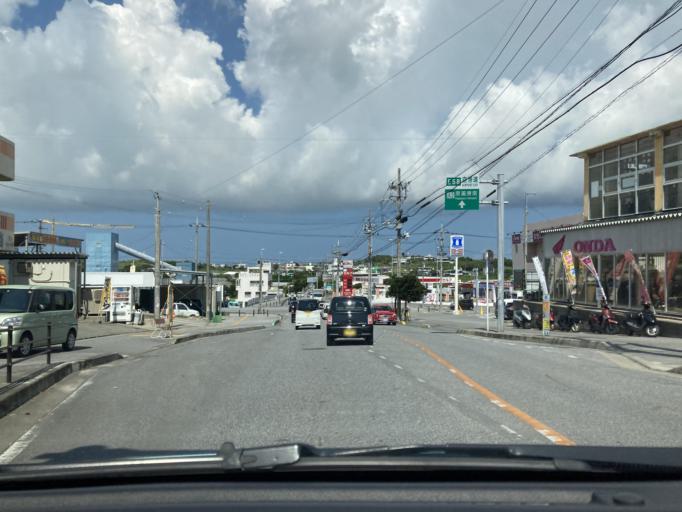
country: JP
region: Okinawa
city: Tomigusuku
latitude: 26.1687
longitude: 127.7404
